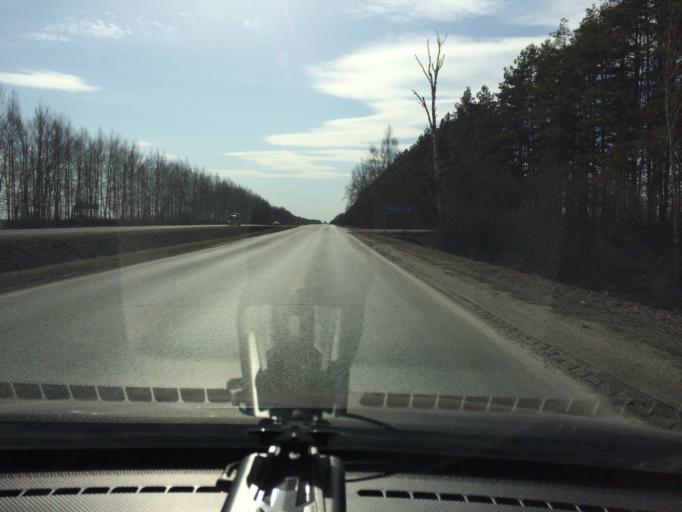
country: RU
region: Mariy-El
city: Surok
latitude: 56.7380
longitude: 48.1748
